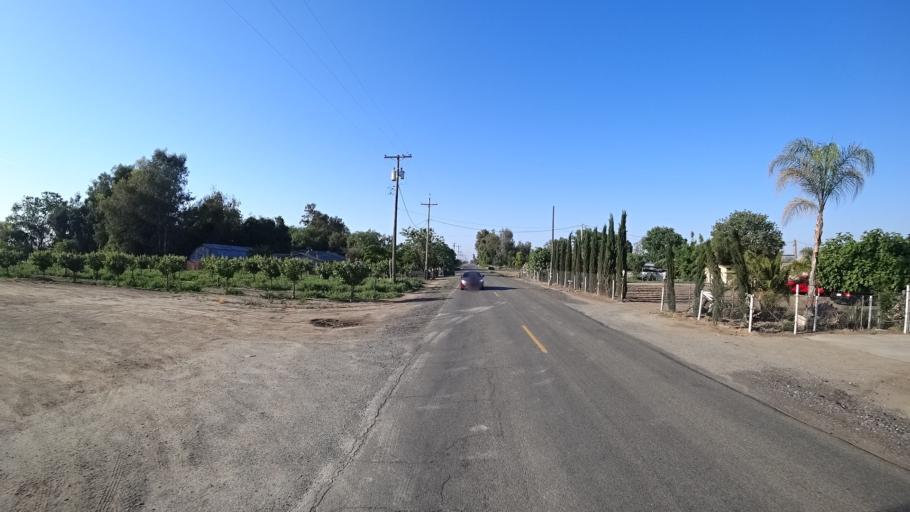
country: US
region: California
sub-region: Kings County
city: Lemoore
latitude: 36.2801
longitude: -119.7447
